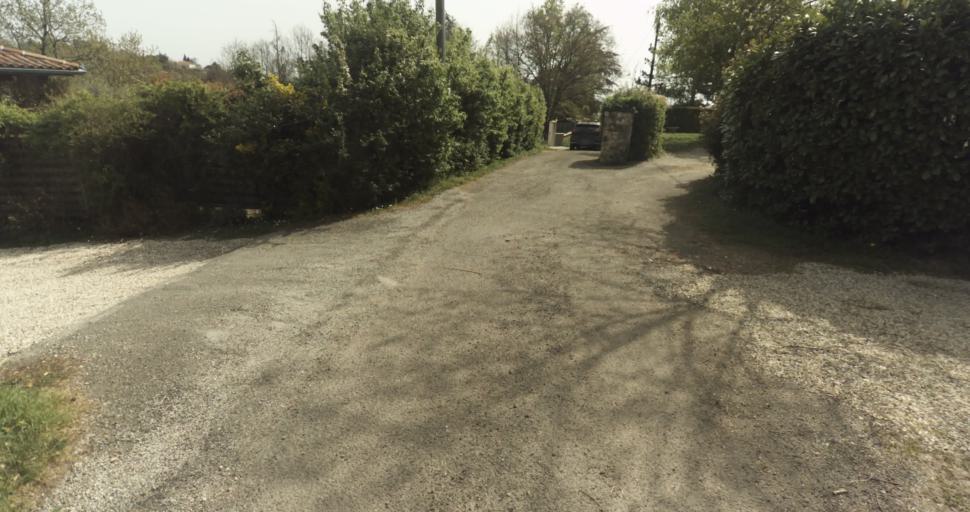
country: FR
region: Midi-Pyrenees
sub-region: Departement du Tarn-et-Garonne
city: Moissac
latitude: 44.1080
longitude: 1.0877
